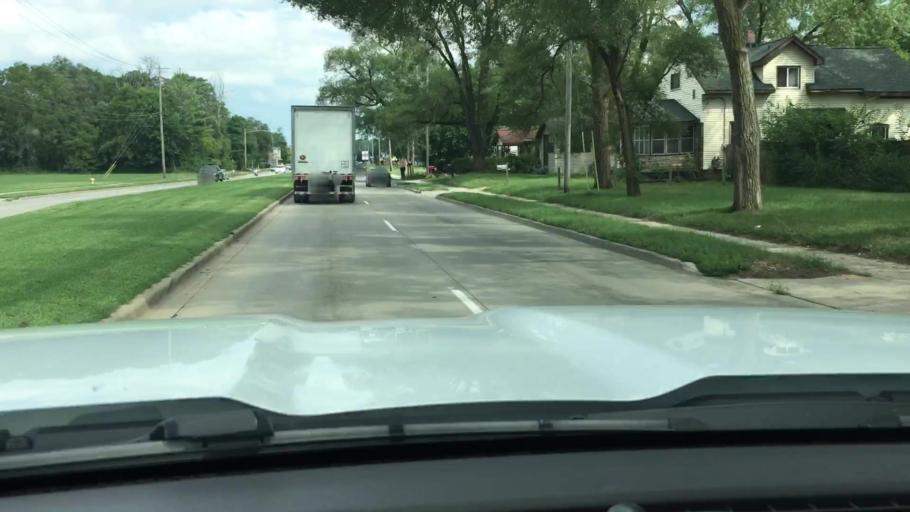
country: US
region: Michigan
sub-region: Kent County
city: Kentwood
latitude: 42.8839
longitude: -85.6590
